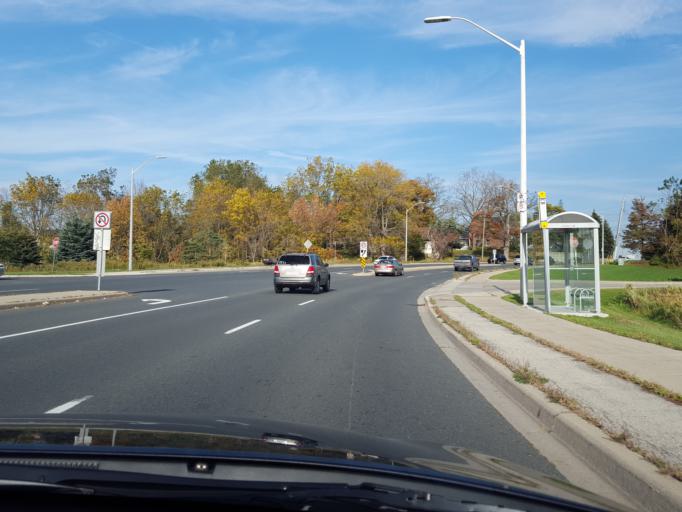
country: CA
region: Ontario
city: Ancaster
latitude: 43.2324
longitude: -79.9343
